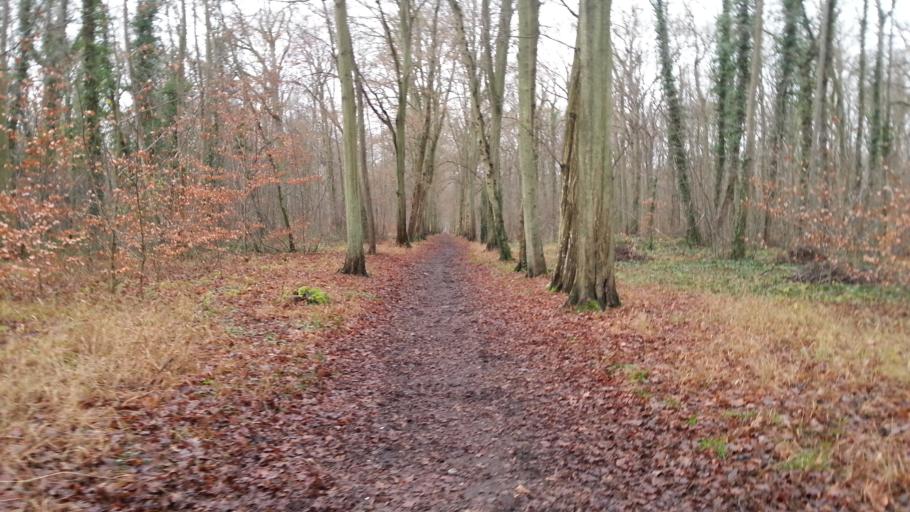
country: FR
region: Picardie
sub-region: Departement de l'Oise
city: Gouvieux
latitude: 49.1858
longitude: 2.3975
